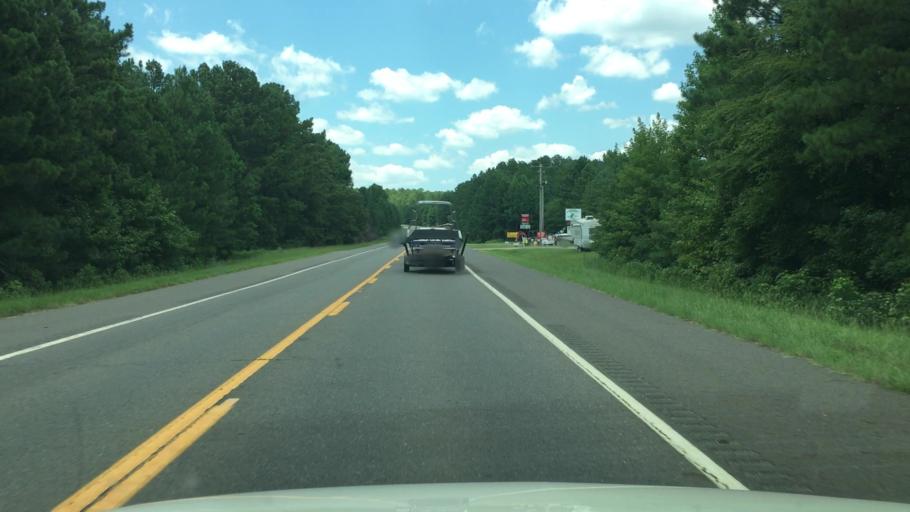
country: US
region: Arkansas
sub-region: Clark County
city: Arkadelphia
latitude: 34.2047
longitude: -93.0787
